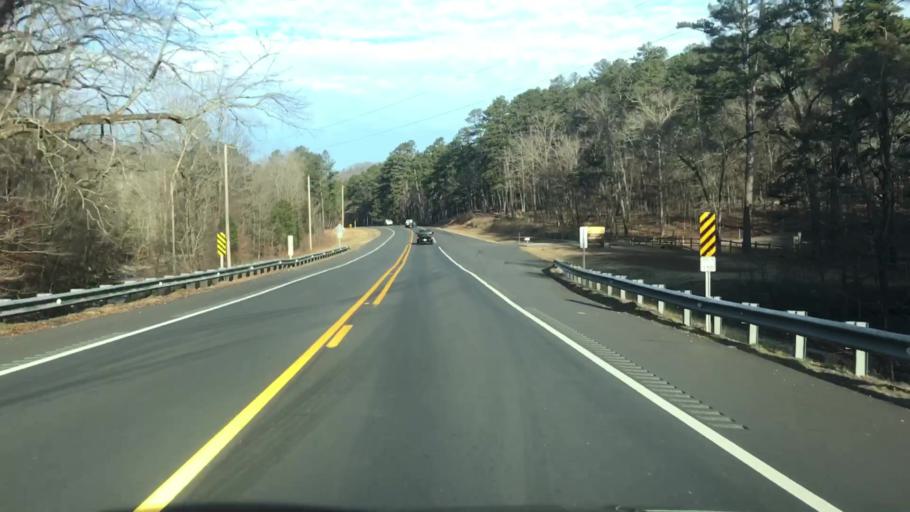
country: US
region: Arkansas
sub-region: Pike County
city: Glenwood
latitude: 34.5153
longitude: -93.3834
